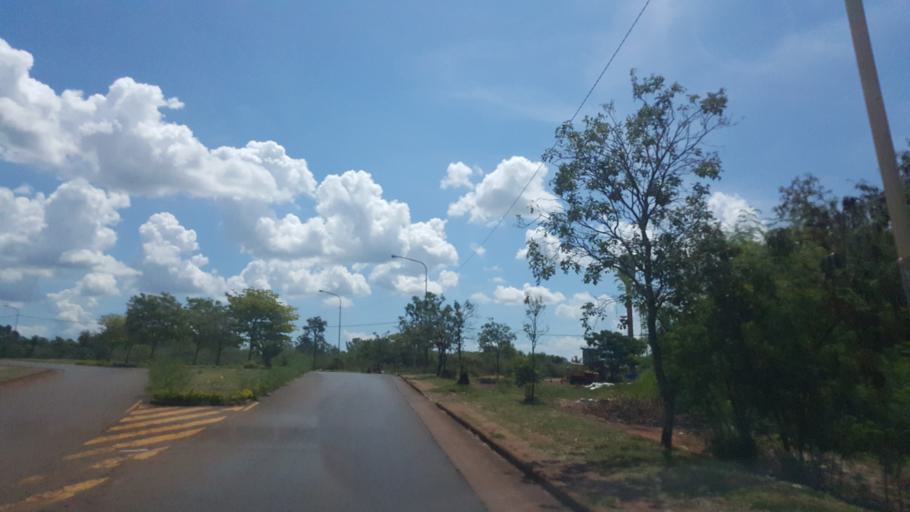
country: AR
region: Misiones
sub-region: Departamento de Capital
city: Posadas
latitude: -27.3734
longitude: -55.9600
